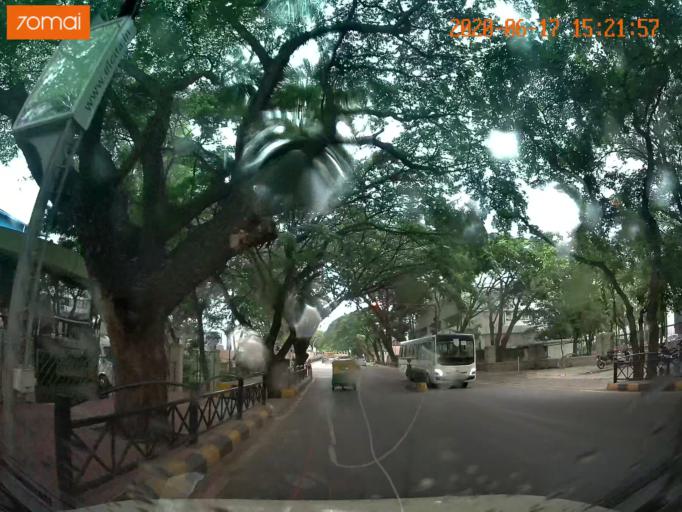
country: IN
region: Karnataka
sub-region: Bangalore Urban
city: Anekal
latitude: 12.8439
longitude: 77.6604
